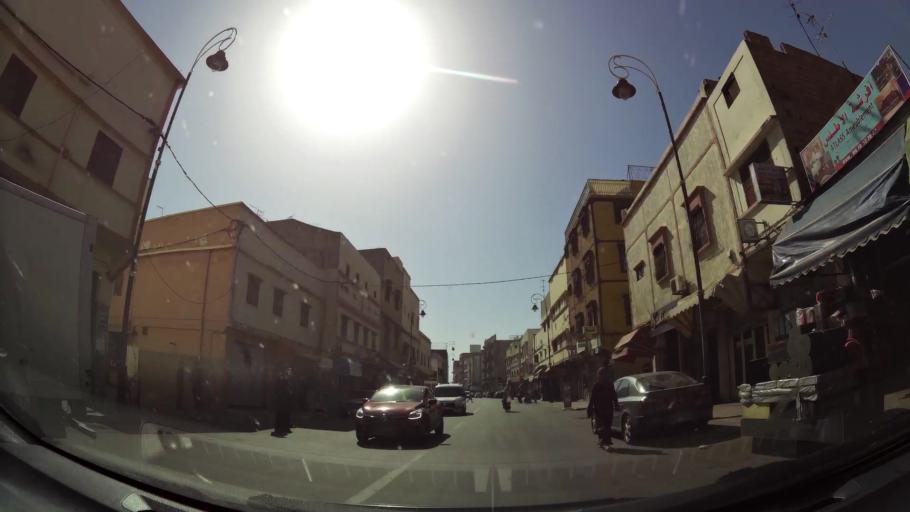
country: MA
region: Souss-Massa-Draa
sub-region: Inezgane-Ait Mellou
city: Inezgane
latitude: 30.3717
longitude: -9.5431
